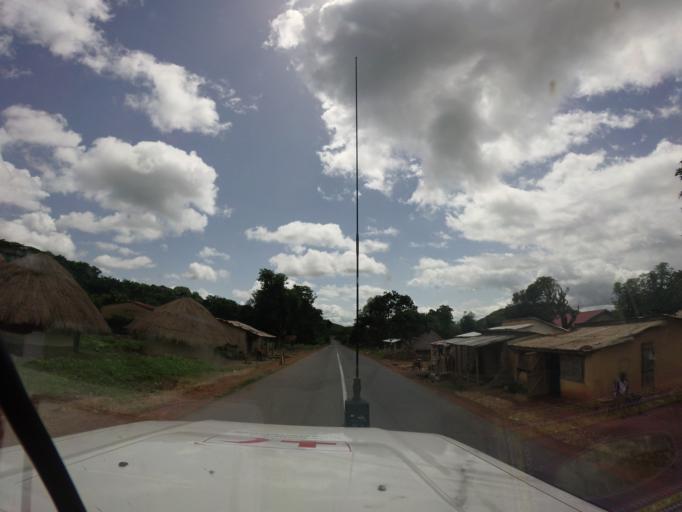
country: SL
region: Northern Province
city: Bindi
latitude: 10.1809
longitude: -11.7288
